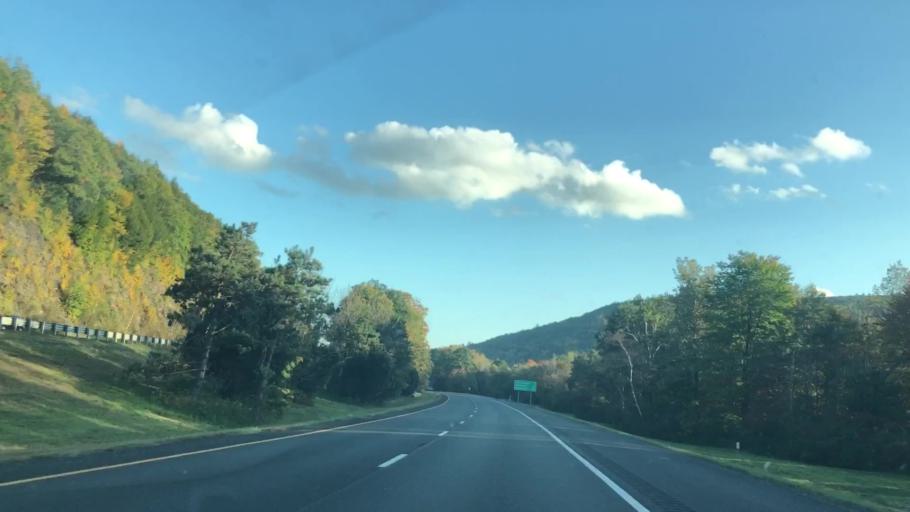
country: US
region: Massachusetts
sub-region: Franklin County
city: Bernardston
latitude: 42.7121
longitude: -72.5655
